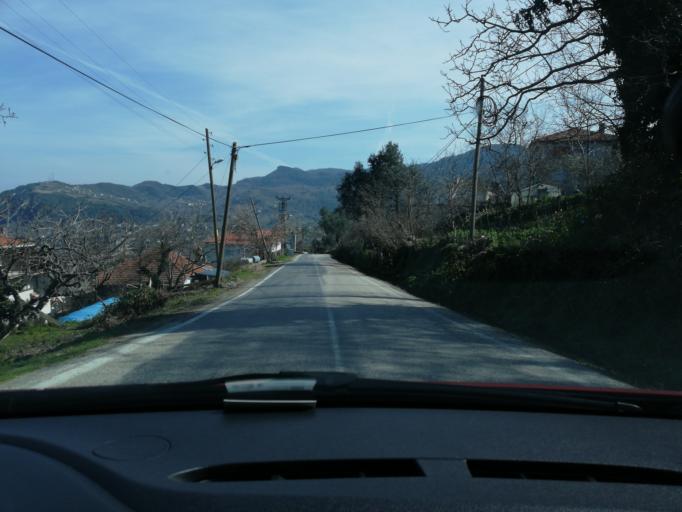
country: TR
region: Bartin
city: Kurucasile
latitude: 41.8277
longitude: 32.6594
